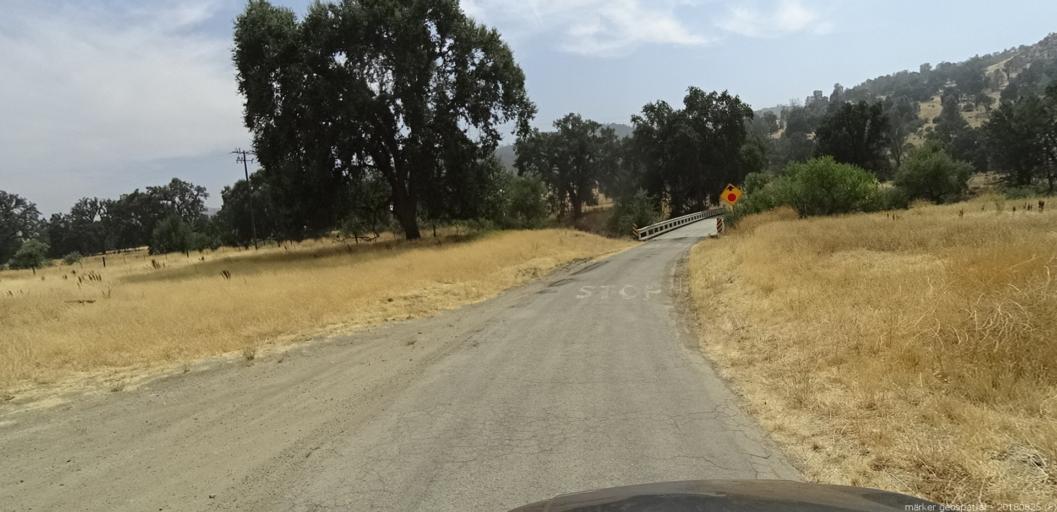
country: US
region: California
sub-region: Fresno County
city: Coalinga
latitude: 36.1953
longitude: -120.7076
